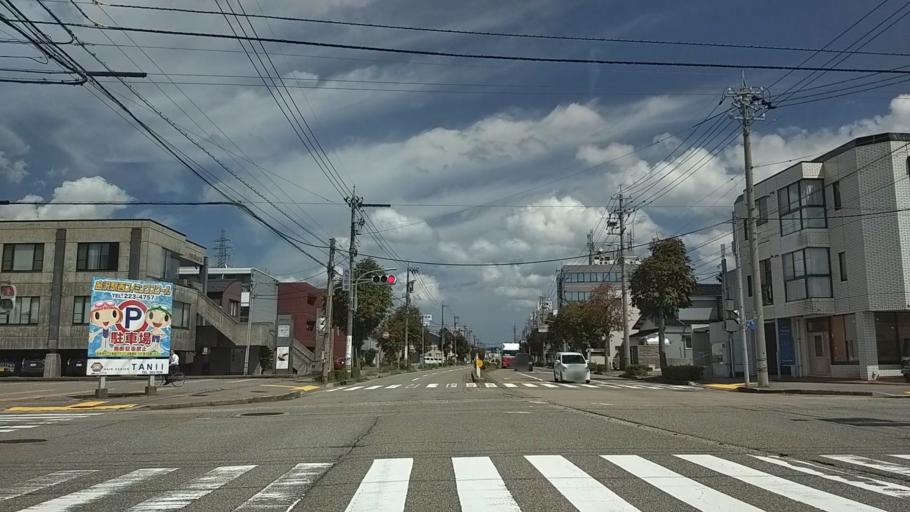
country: JP
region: Ishikawa
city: Kanazawa-shi
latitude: 36.5850
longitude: 136.6435
